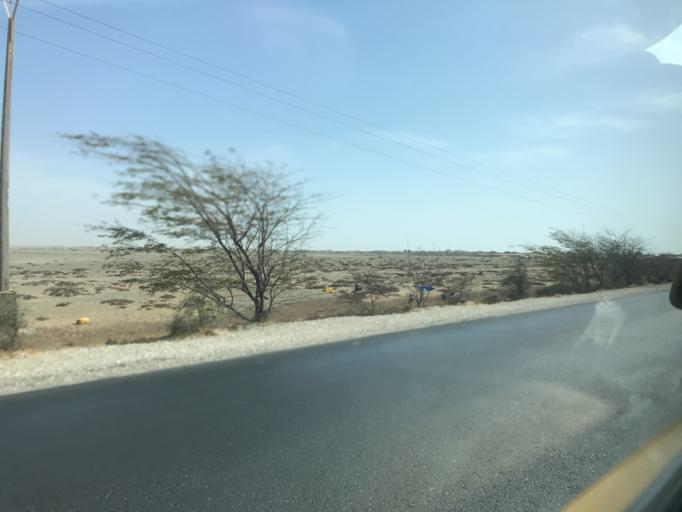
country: SN
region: Saint-Louis
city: Saint-Louis
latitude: 16.0394
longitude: -16.4512
